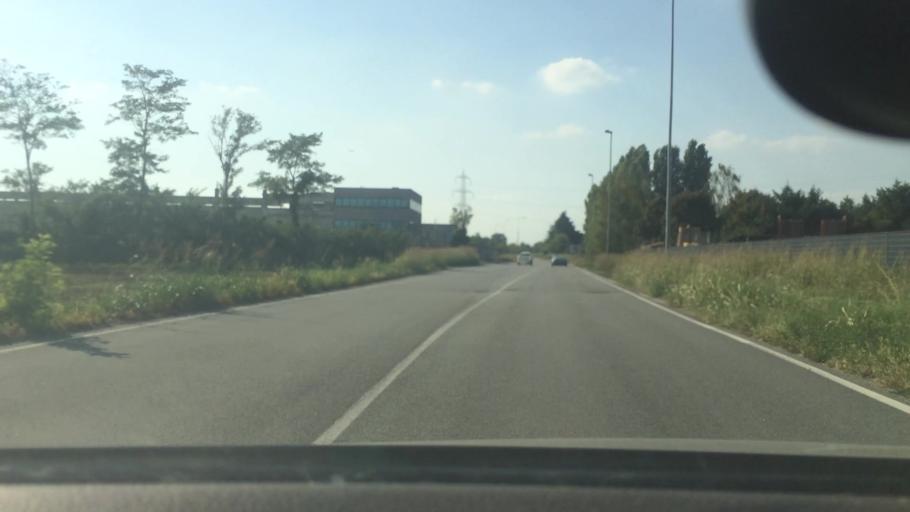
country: IT
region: Lombardy
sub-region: Citta metropolitana di Milano
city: Buscate
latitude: 45.5352
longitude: 8.8139
